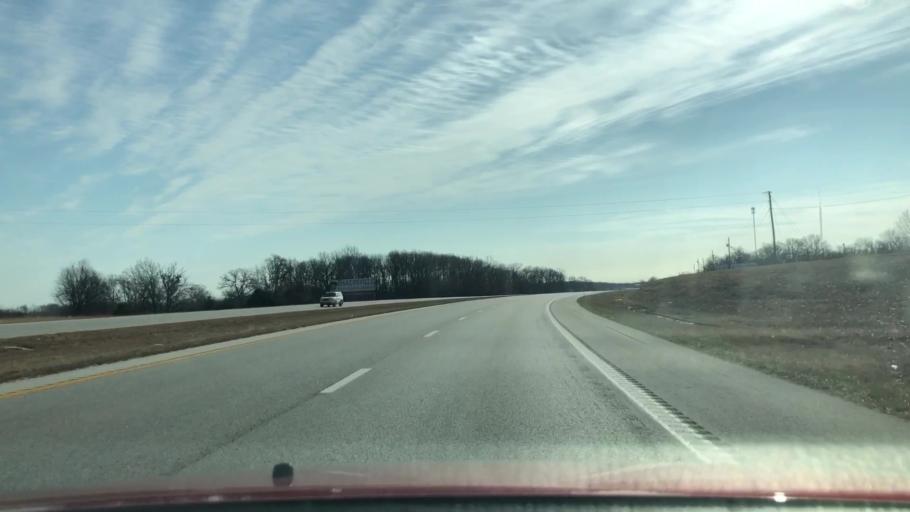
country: US
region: Missouri
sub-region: Webster County
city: Seymour
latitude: 37.1448
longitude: -92.7487
